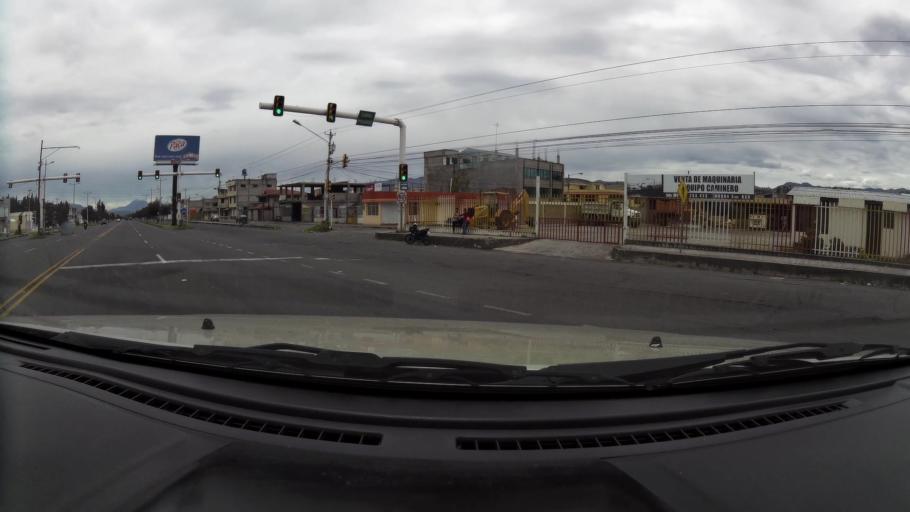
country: EC
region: Cotopaxi
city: Latacunga
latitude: -0.9674
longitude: -78.6123
